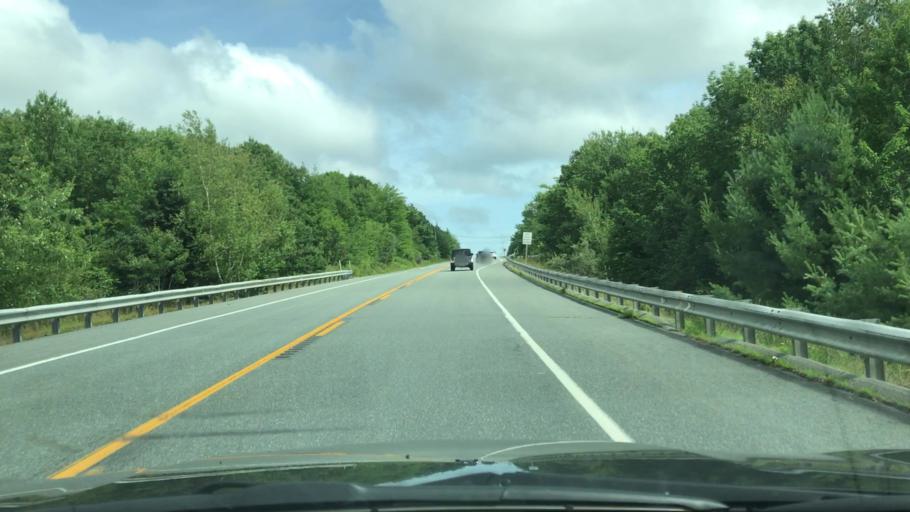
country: US
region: Maine
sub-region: Hancock County
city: Surry
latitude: 44.5557
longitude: -68.5415
